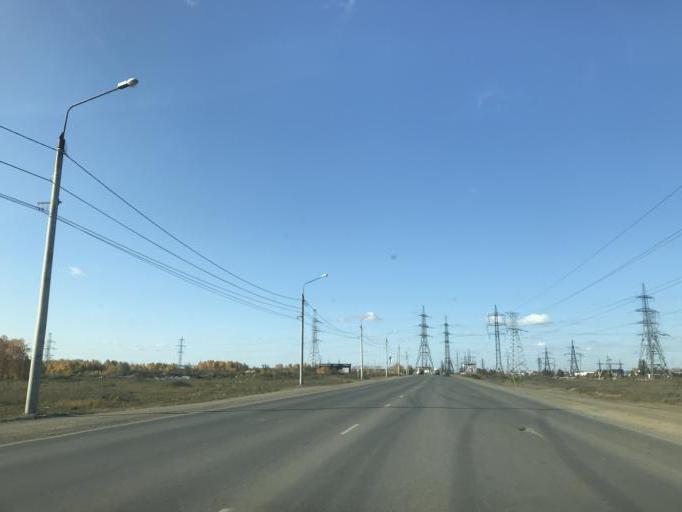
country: RU
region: Chelyabinsk
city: Roshchino
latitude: 55.2230
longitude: 61.2936
